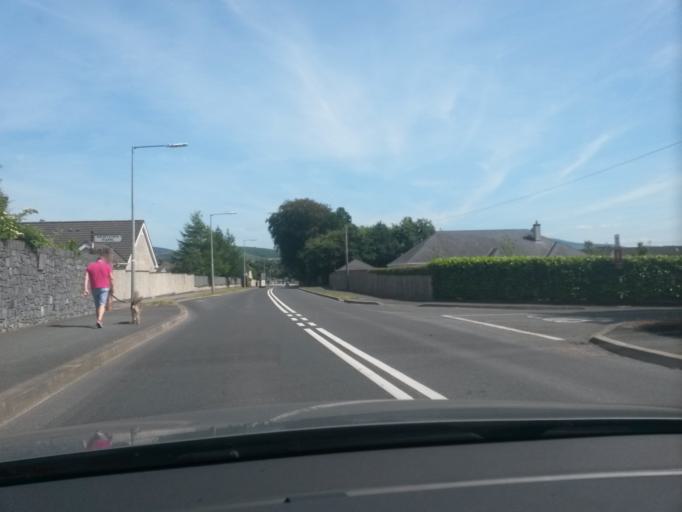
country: IE
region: Leinster
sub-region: Wicklow
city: Blessington
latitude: 53.1725
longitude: -6.5476
